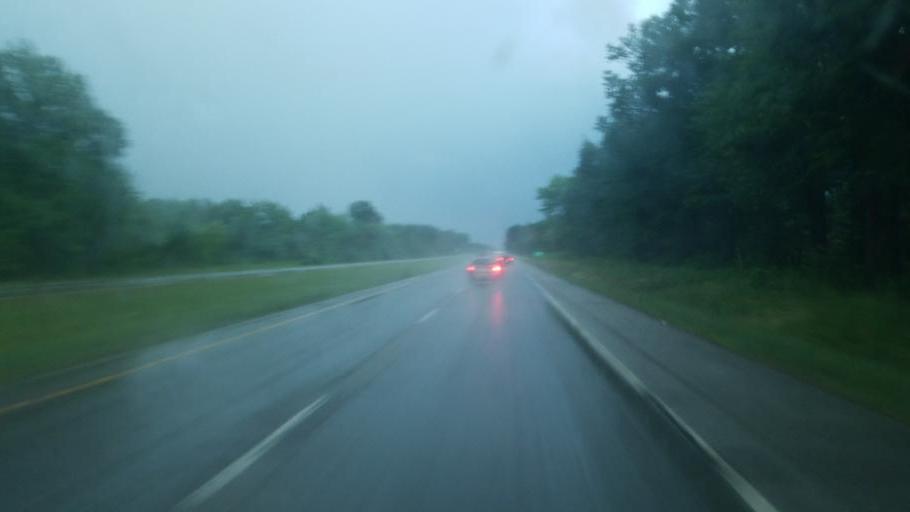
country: US
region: Ohio
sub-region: Wayne County
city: Doylestown
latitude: 40.9814
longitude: -81.6632
